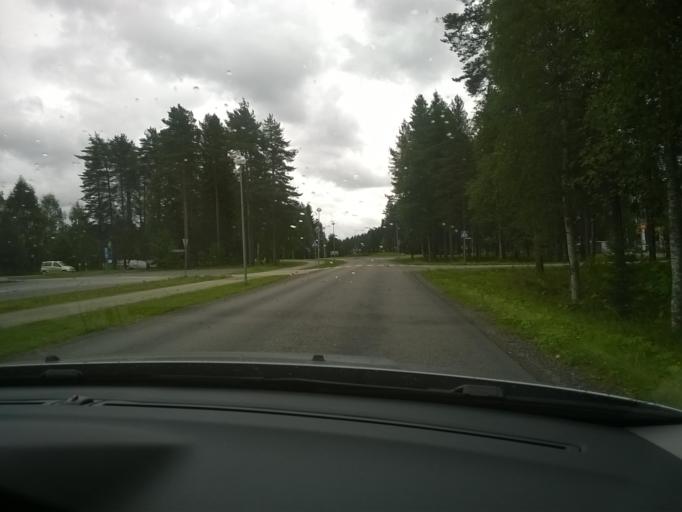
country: FI
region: Kainuu
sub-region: Kehys-Kainuu
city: Kuhmo
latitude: 64.1232
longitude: 29.5058
